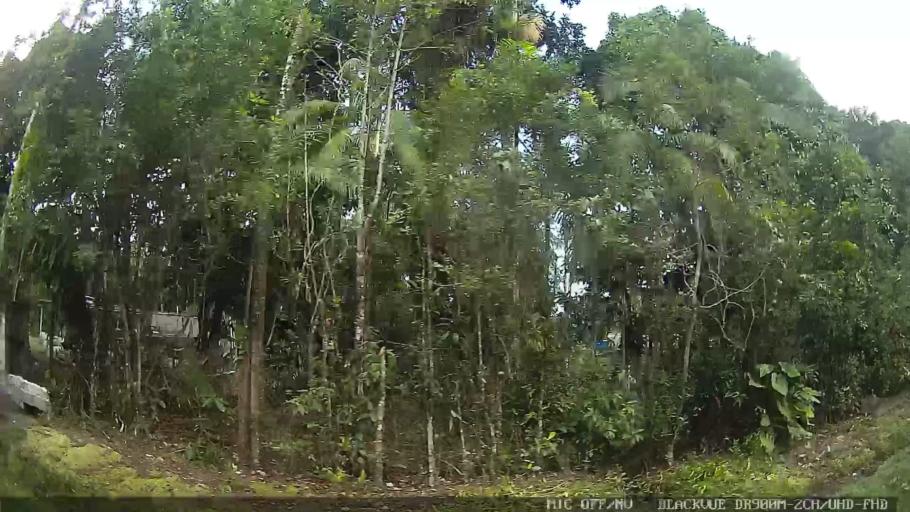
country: BR
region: Sao Paulo
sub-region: Peruibe
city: Peruibe
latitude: -24.1827
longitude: -46.9393
